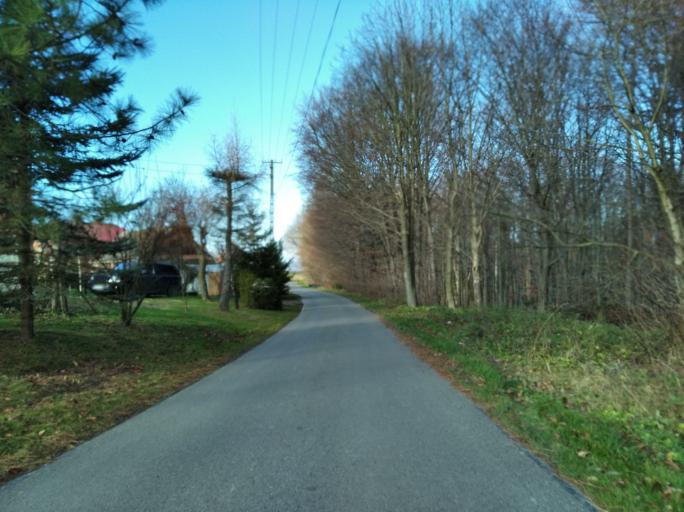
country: PL
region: Subcarpathian Voivodeship
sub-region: Powiat strzyzowski
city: Czudec
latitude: 49.9148
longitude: 21.8450
